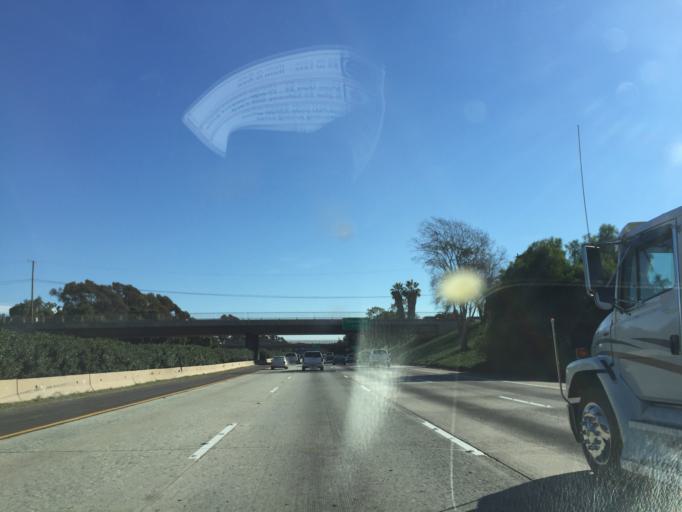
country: US
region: California
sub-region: San Diego County
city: Carlsbad
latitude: 33.1531
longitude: -117.3371
